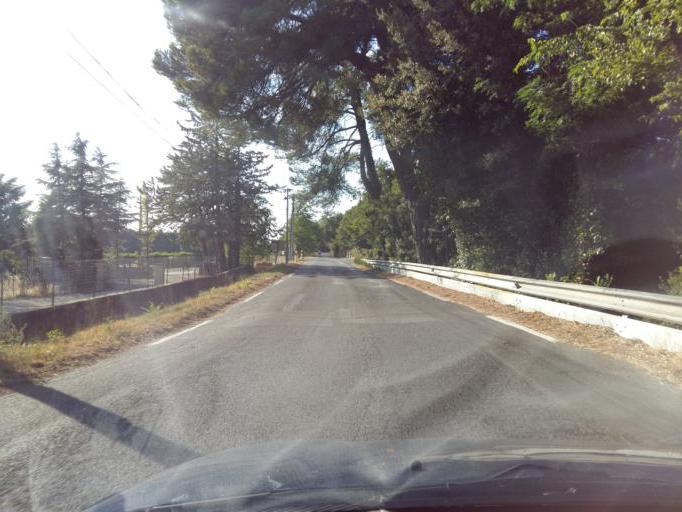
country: FR
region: Provence-Alpes-Cote d'Azur
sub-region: Departement du Vaucluse
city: Saint-Didier
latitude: 44.0153
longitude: 5.1023
